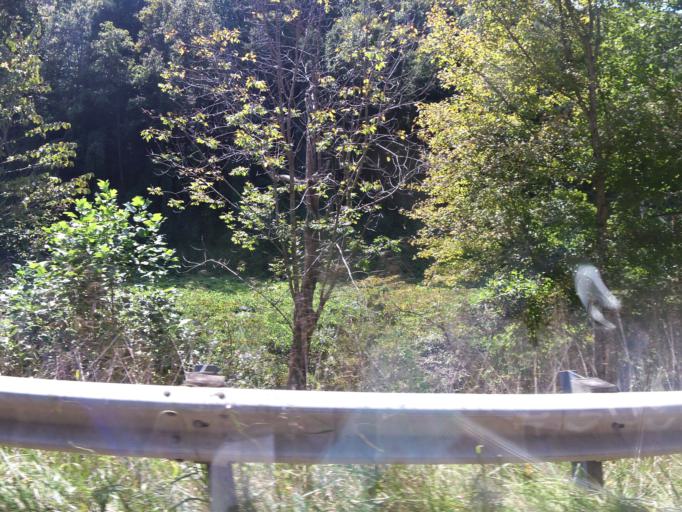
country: US
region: Kentucky
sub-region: Harlan County
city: Loyall
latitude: 36.9993
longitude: -83.3945
